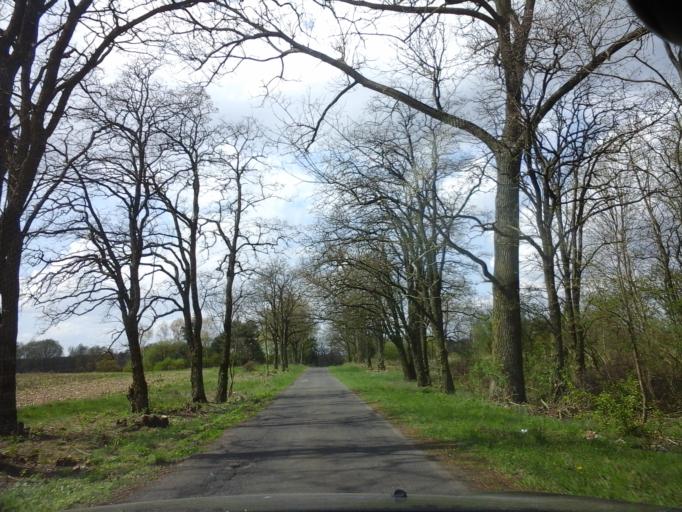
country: PL
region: West Pomeranian Voivodeship
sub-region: Powiat stargardzki
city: Dobrzany
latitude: 53.3328
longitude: 15.4015
